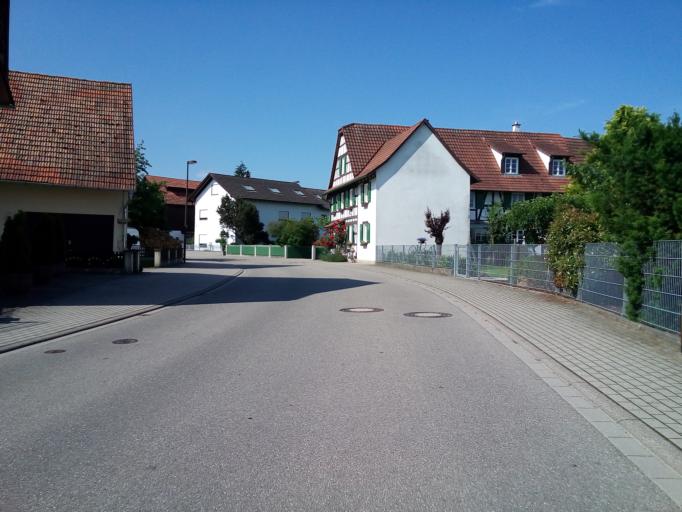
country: DE
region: Baden-Wuerttemberg
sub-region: Freiburg Region
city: Rheinau
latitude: 48.6275
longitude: 7.9205
